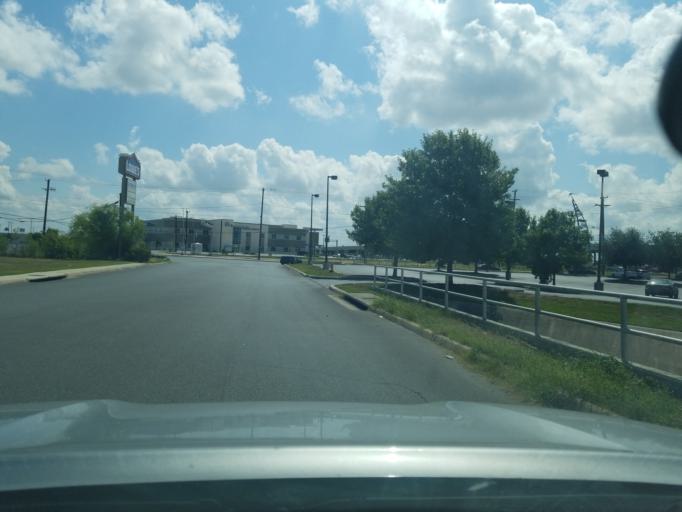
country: US
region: Texas
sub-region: Bexar County
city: San Antonio
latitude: 29.3521
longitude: -98.5353
